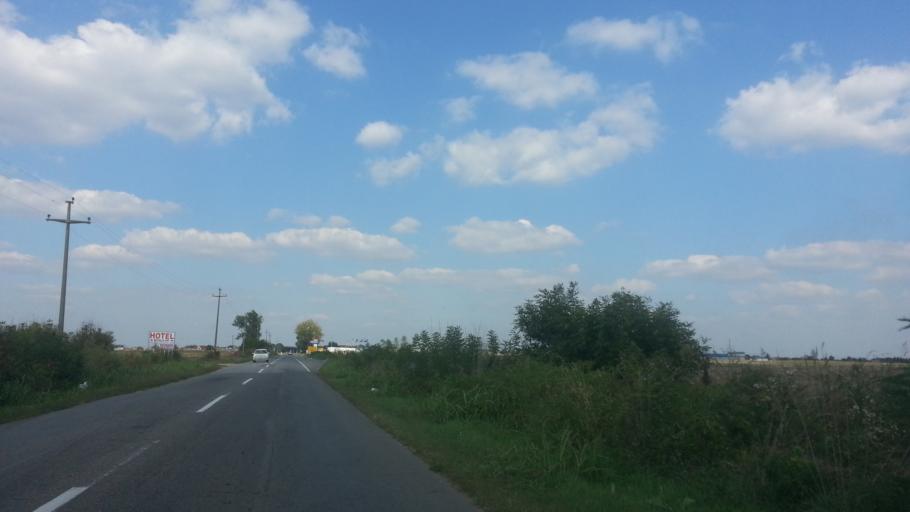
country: RS
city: Novi Banovci
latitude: 44.9370
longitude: 20.2808
